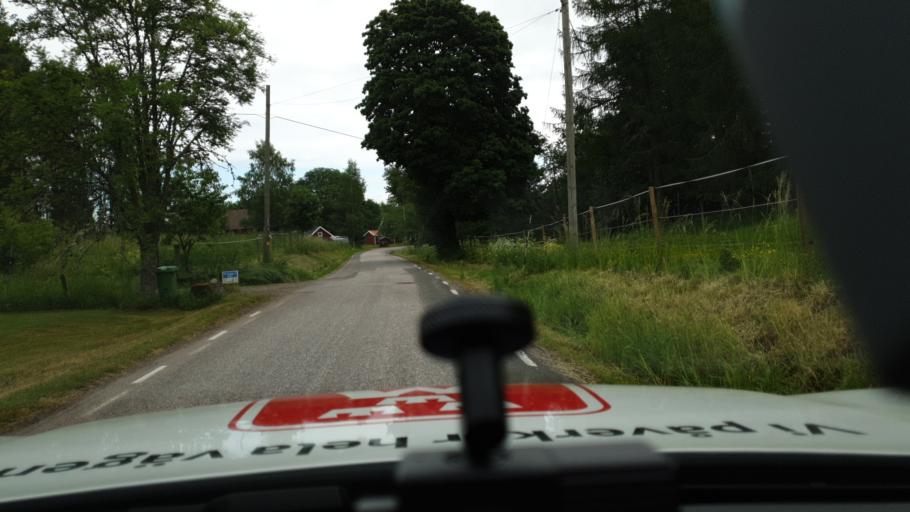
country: SE
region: Vaestra Goetaland
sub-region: Karlsborgs Kommun
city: Molltorp
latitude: 58.4208
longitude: 14.3548
